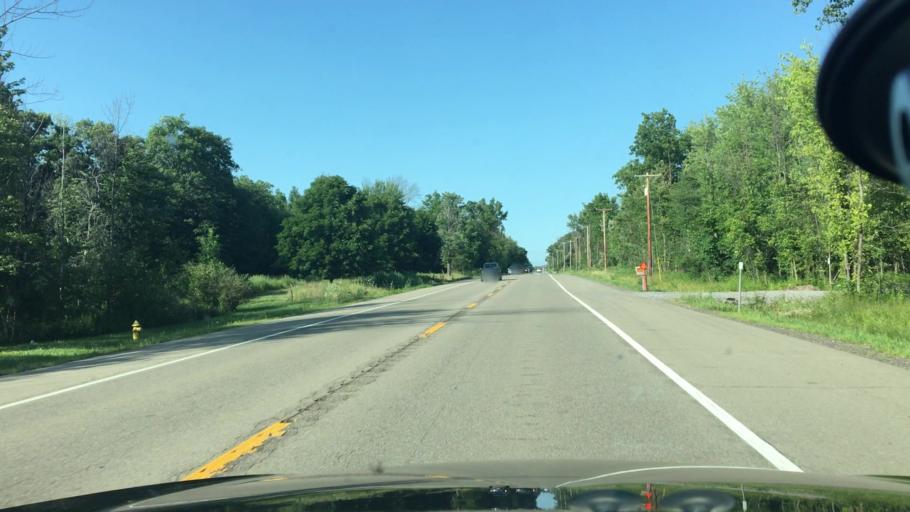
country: US
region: New York
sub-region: Erie County
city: Angola
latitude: 42.6638
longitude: -78.9680
